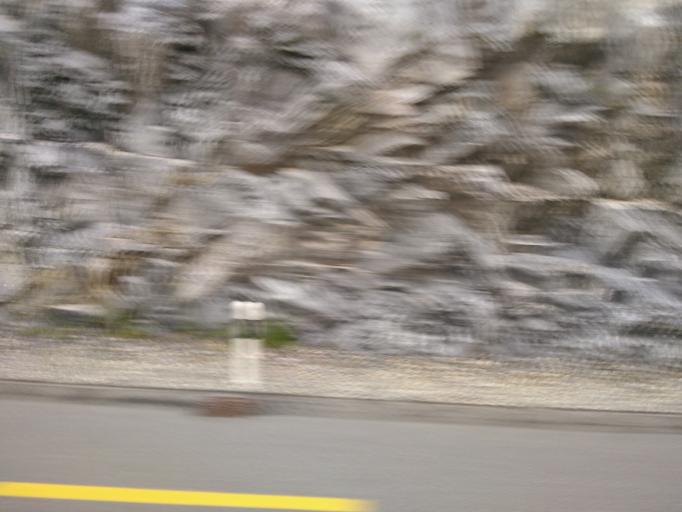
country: CH
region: Grisons
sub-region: Imboden District
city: Flims
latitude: 46.8342
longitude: 9.3255
